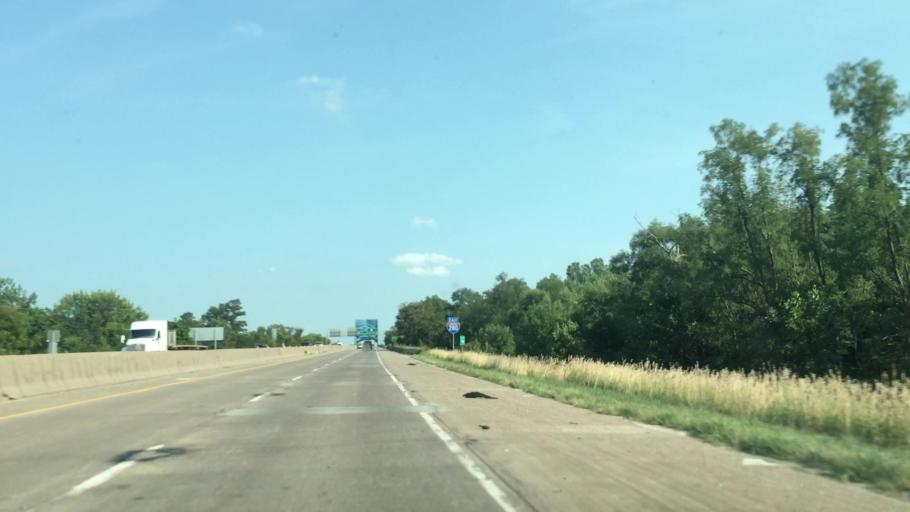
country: US
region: Illinois
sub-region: Rock Island County
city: Rock Island
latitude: 41.4864
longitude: -90.6421
